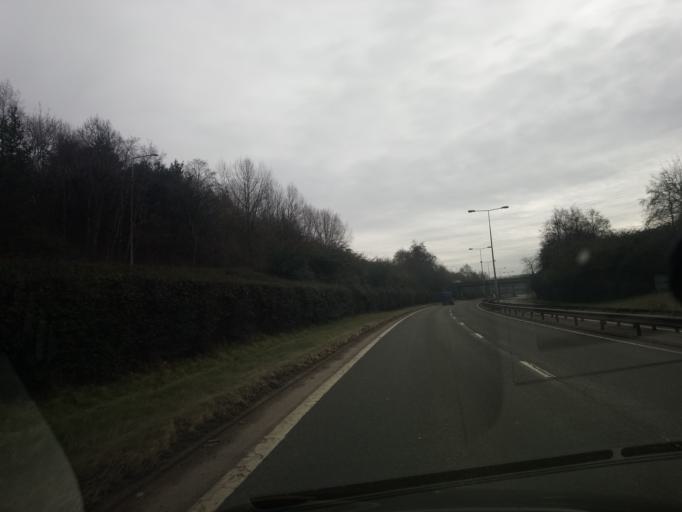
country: GB
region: England
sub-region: Telford and Wrekin
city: Oakengates
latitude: 52.7061
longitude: -2.4606
